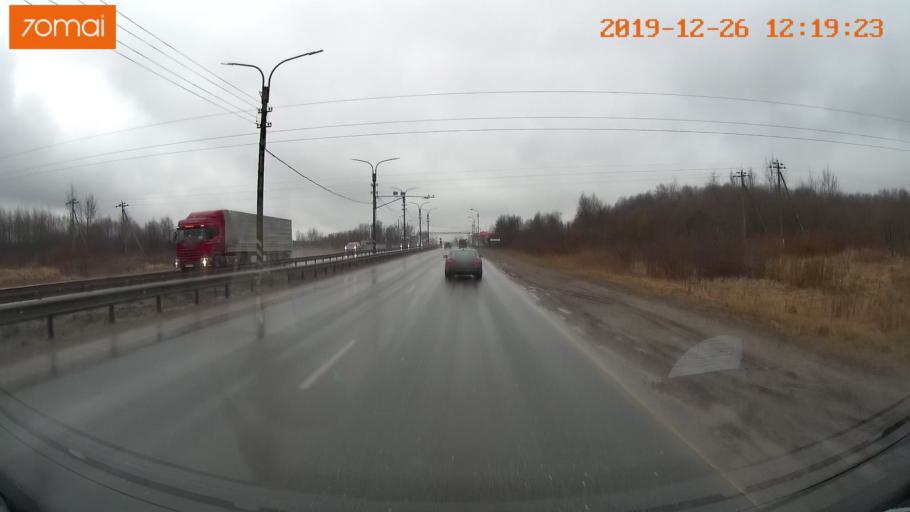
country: RU
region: Vologda
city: Tonshalovo
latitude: 59.1684
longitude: 37.9378
